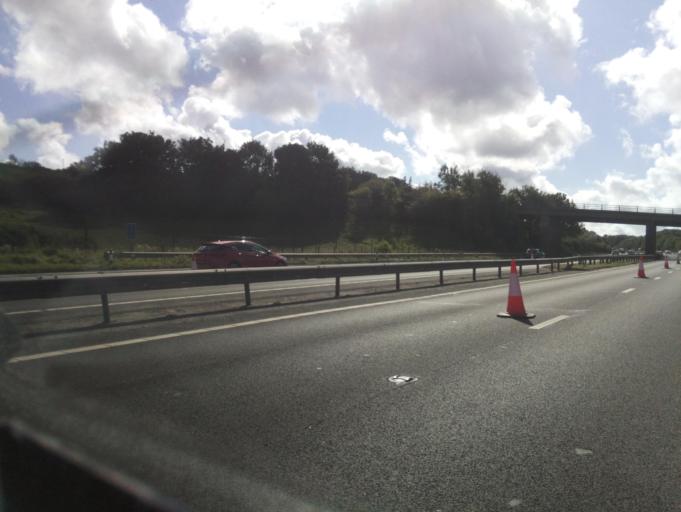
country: GB
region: England
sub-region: Lancashire
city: Carnforth
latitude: 54.1251
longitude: -2.7545
